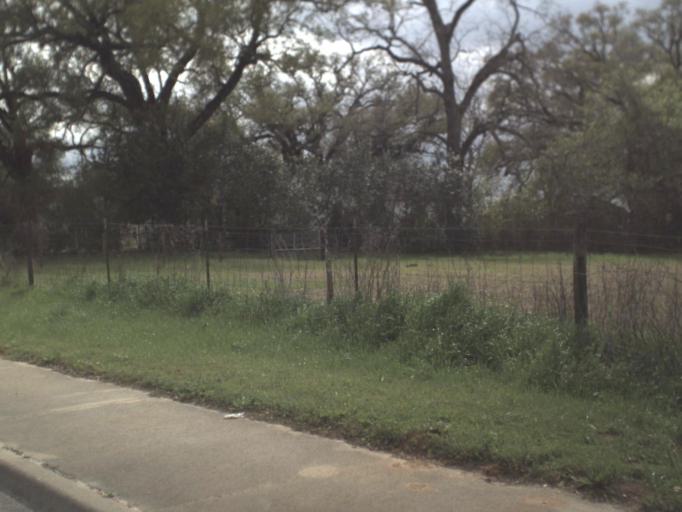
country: US
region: Florida
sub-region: Gadsden County
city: Quincy
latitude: 30.5674
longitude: -84.5932
